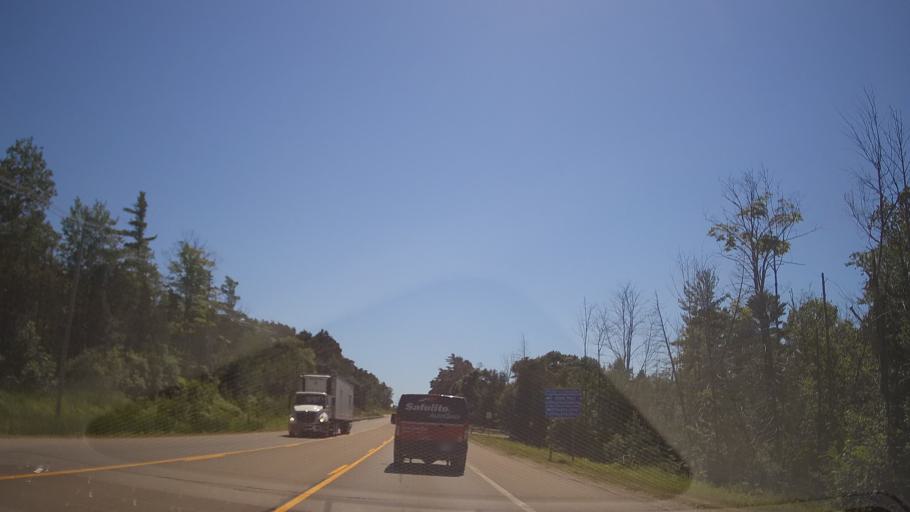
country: US
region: Michigan
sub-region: Emmet County
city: Petoskey
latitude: 45.3938
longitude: -84.8977
